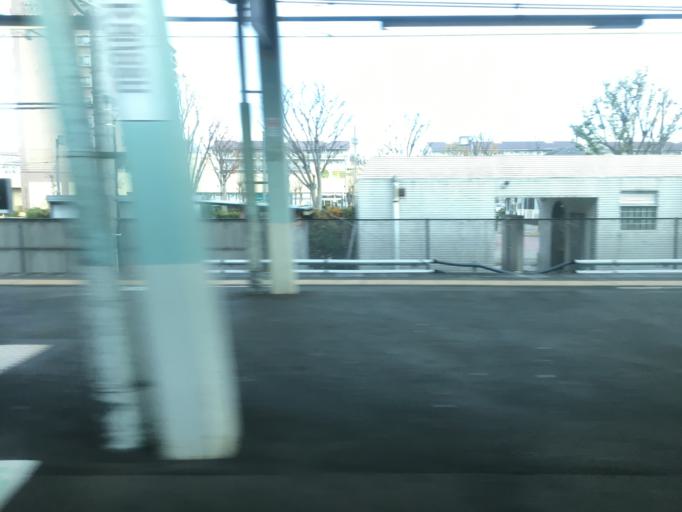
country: JP
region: Saitama
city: Fukiage-fujimi
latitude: 36.0853
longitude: 139.4773
